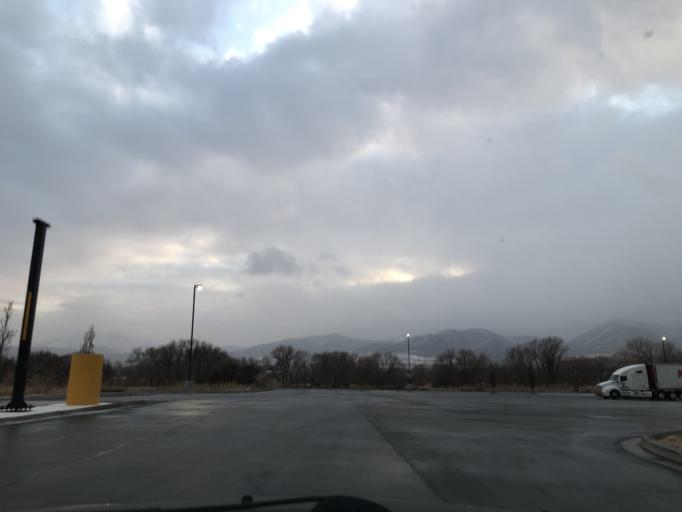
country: US
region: Utah
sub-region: Cache County
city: Wellsville
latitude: 41.6437
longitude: -111.9131
